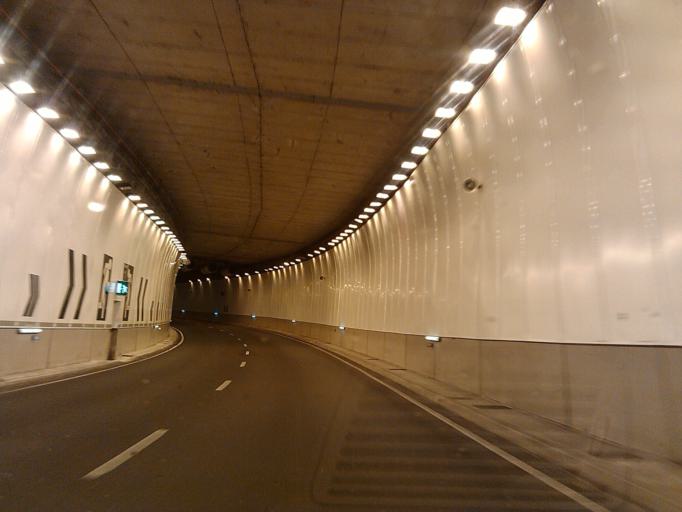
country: ES
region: Galicia
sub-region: Provincia da Coruna
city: Santiago de Compostela
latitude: 42.8697
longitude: -8.5482
